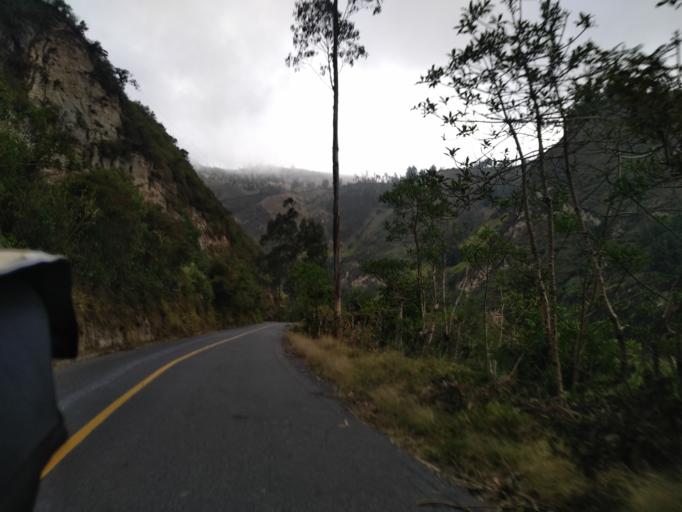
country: EC
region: Cotopaxi
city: Saquisili
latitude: -0.6899
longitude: -78.8665
